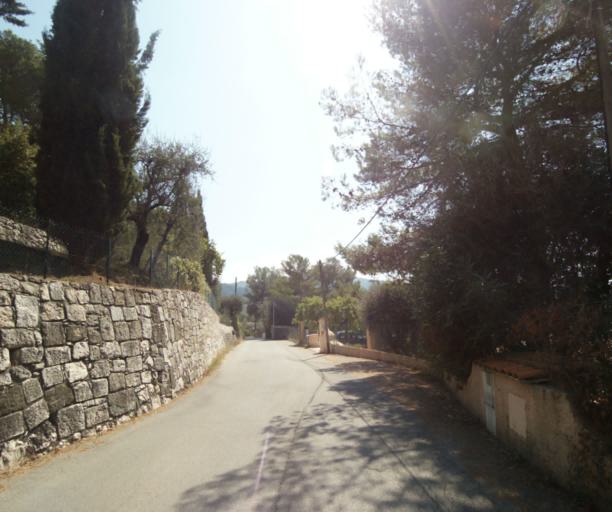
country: FR
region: Provence-Alpes-Cote d'Azur
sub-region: Departement des Alpes-Maritimes
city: Drap
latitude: 43.7571
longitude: 7.3246
